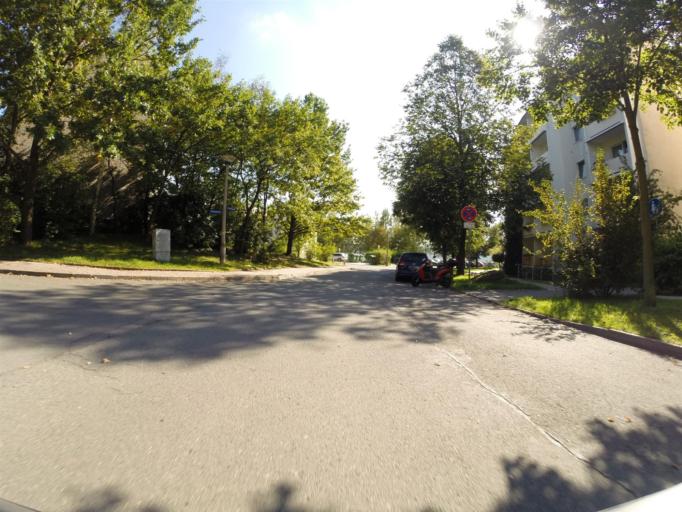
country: DE
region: Thuringia
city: Zollnitz
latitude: 50.8812
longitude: 11.6368
